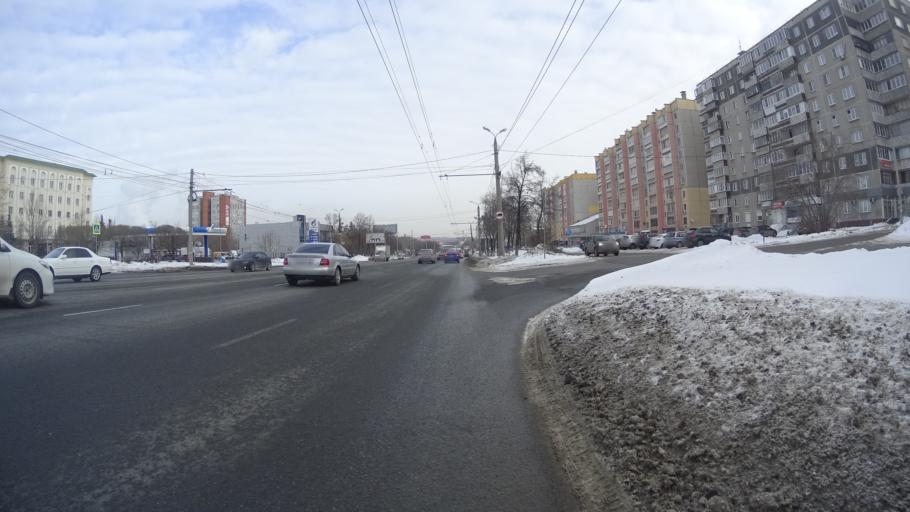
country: RU
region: Chelyabinsk
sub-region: Gorod Chelyabinsk
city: Chelyabinsk
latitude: 55.1920
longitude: 61.3816
